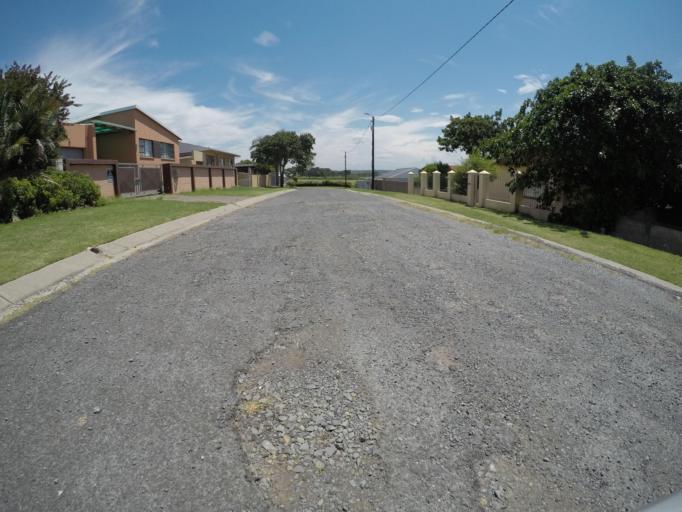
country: ZA
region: Eastern Cape
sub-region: Buffalo City Metropolitan Municipality
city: East London
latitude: -33.0345
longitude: 27.8507
